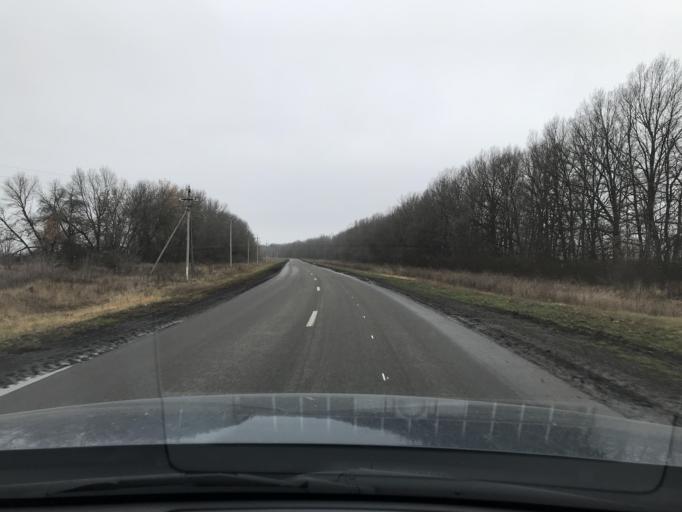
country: RU
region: Penza
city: Zemetchino
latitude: 53.5414
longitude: 42.6674
